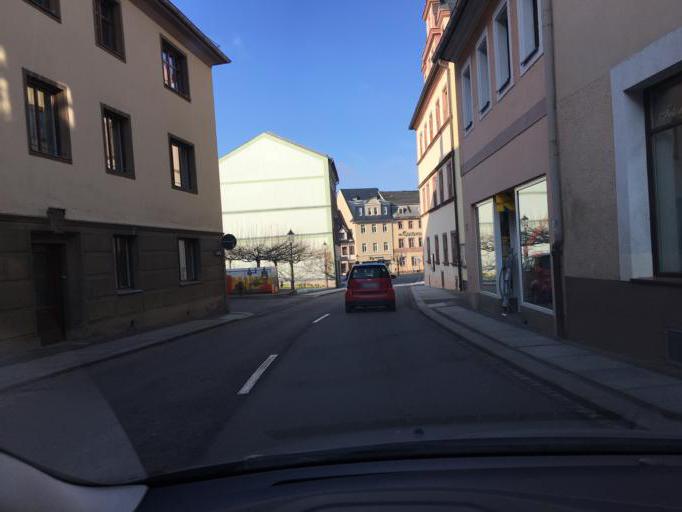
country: DE
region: Saxony
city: Penig
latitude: 50.9328
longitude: 12.7060
